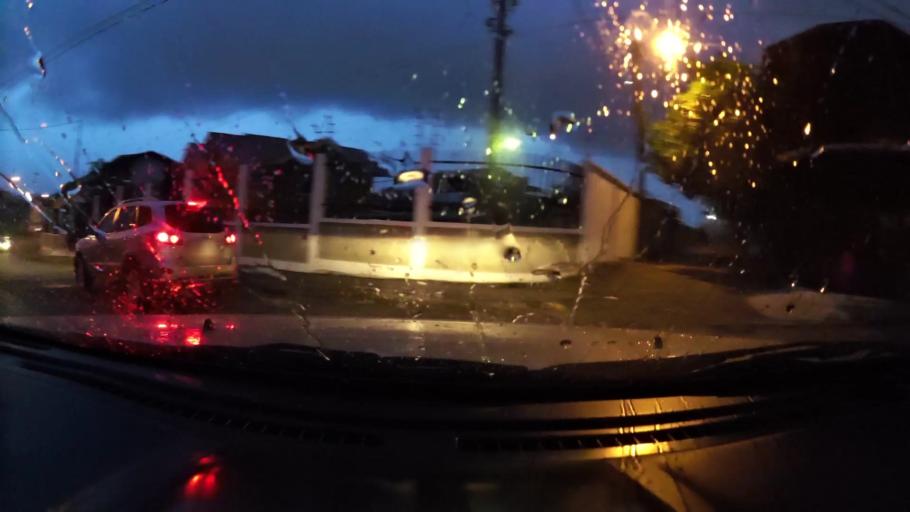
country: EC
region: Pastaza
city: Puyo
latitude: -1.4845
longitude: -78.0035
